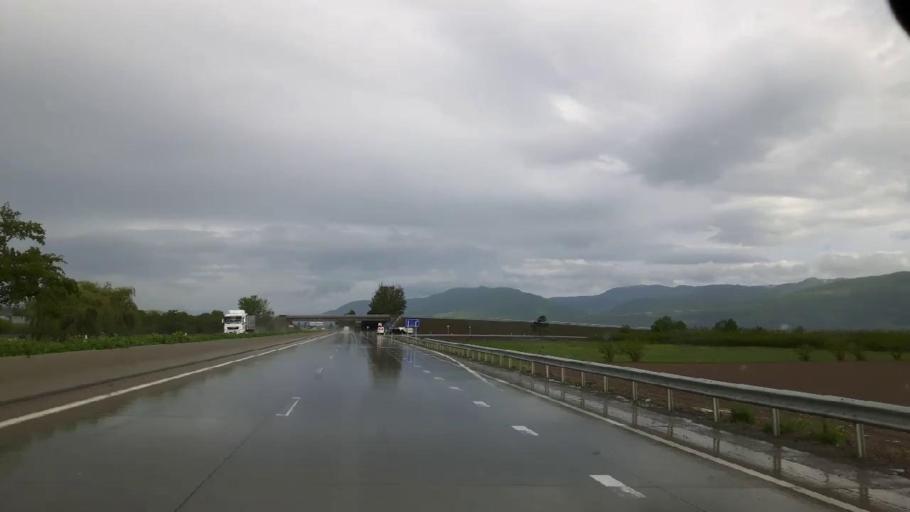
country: GE
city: Agara
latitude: 42.0328
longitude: 43.9466
